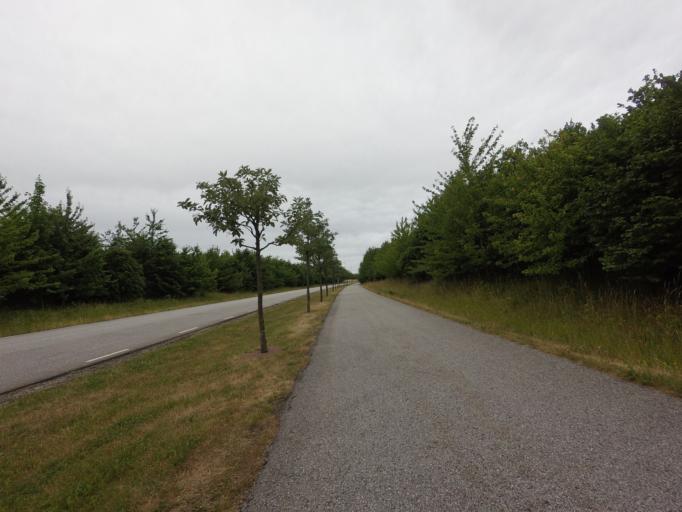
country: SE
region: Skane
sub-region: Malmo
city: Bunkeflostrand
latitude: 55.5669
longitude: 12.9158
